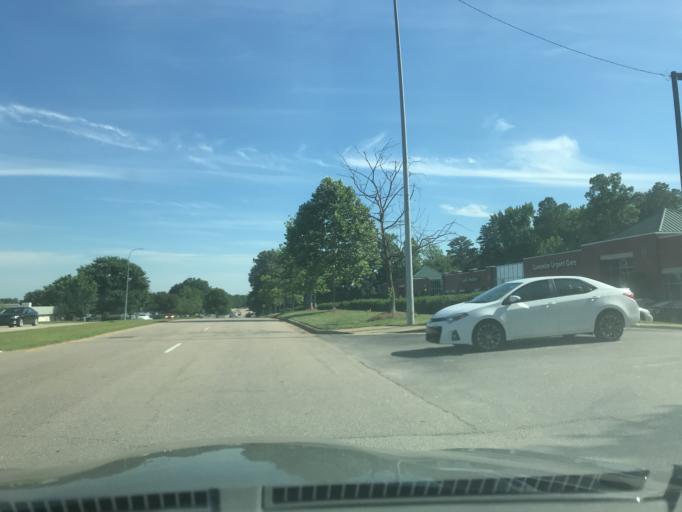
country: US
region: North Carolina
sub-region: Wake County
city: Raleigh
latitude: 35.8532
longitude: -78.5863
